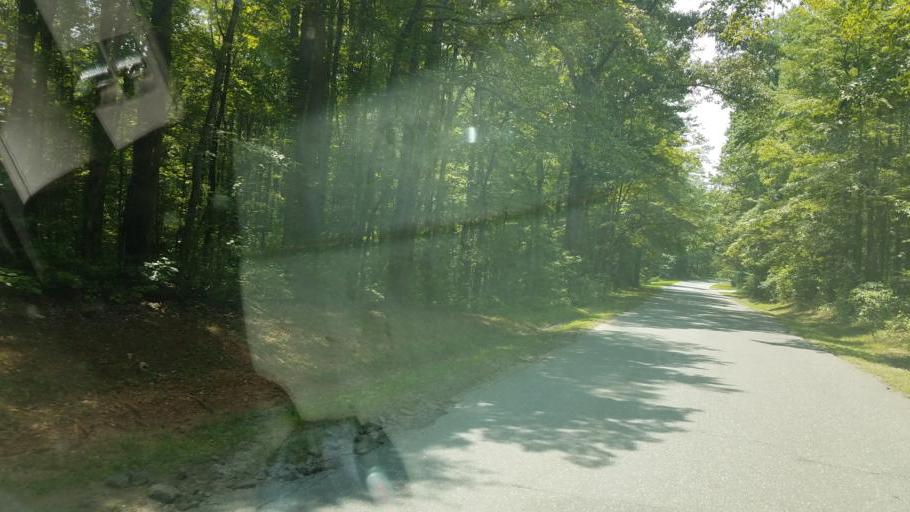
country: US
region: North Carolina
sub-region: Cleveland County
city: Kings Mountain
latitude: 35.1579
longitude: -81.3287
